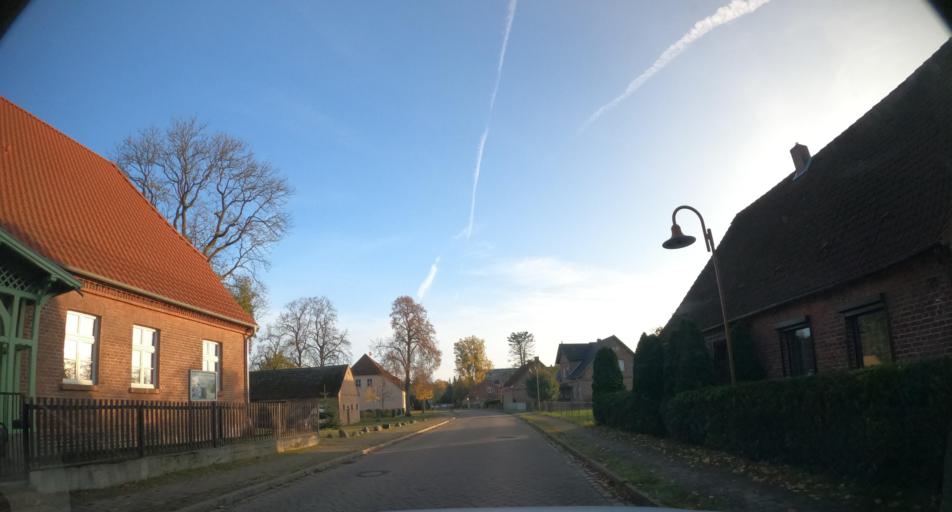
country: DE
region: Mecklenburg-Vorpommern
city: Ahlbeck
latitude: 53.6709
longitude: 14.1889
